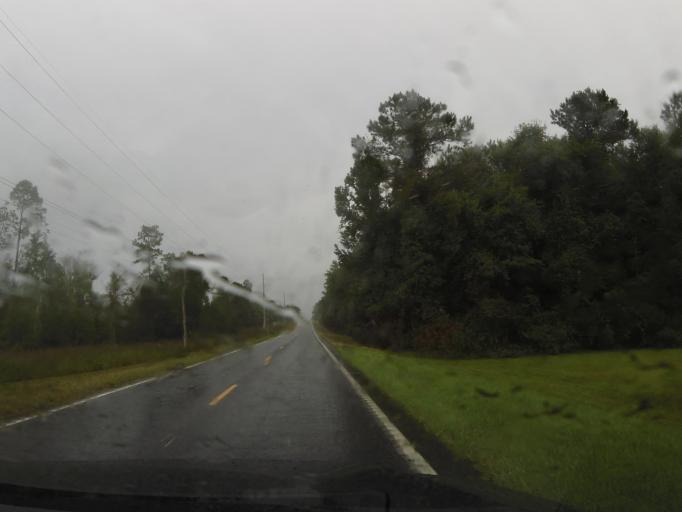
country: US
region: Florida
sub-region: Baker County
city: Macclenny
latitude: 30.3881
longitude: -82.1281
